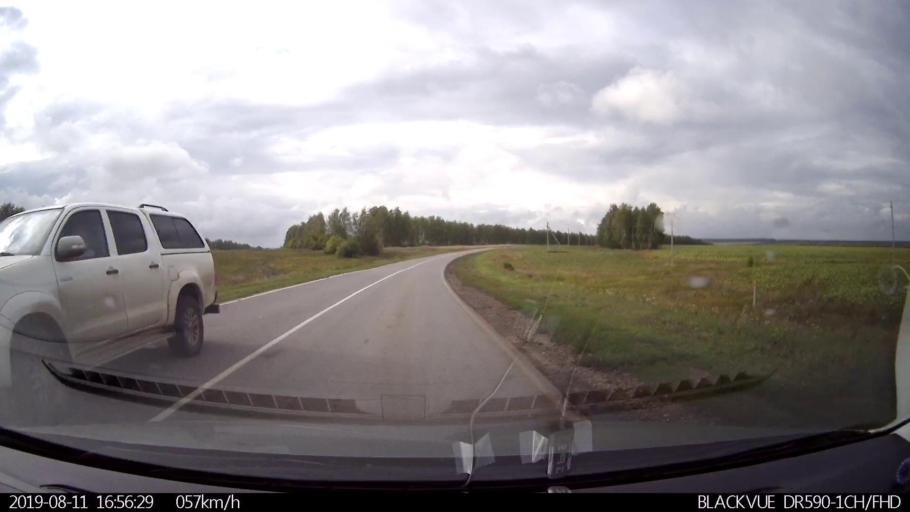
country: RU
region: Ulyanovsk
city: Mayna
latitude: 54.2880
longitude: 47.6533
